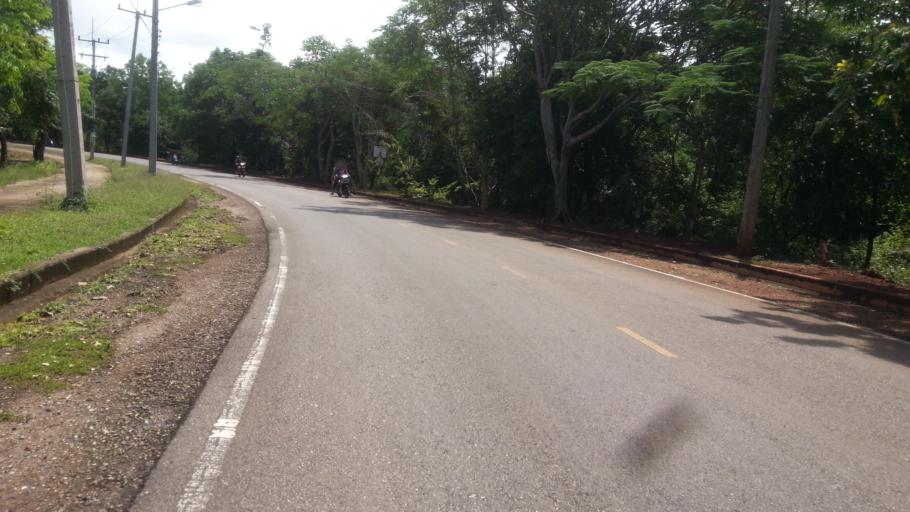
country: TH
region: Kanchanaburi
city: Sai Yok
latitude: 14.1283
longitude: 99.1589
